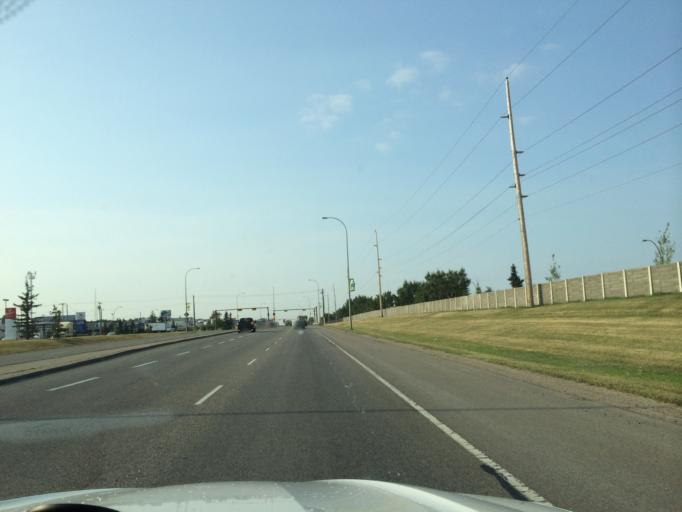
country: CA
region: Alberta
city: Calgary
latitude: 51.0606
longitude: -114.0019
